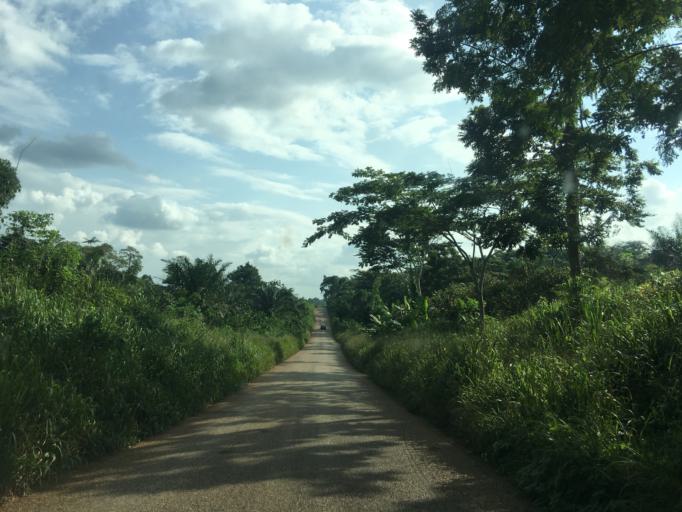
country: GH
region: Western
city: Bibiani
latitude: 6.7684
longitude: -2.5723
